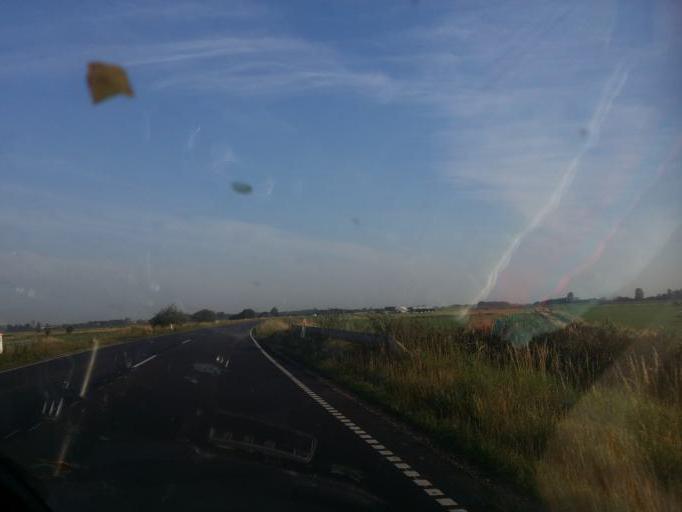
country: DK
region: South Denmark
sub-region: Tonder Kommune
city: Tonder
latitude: 54.9173
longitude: 8.8966
